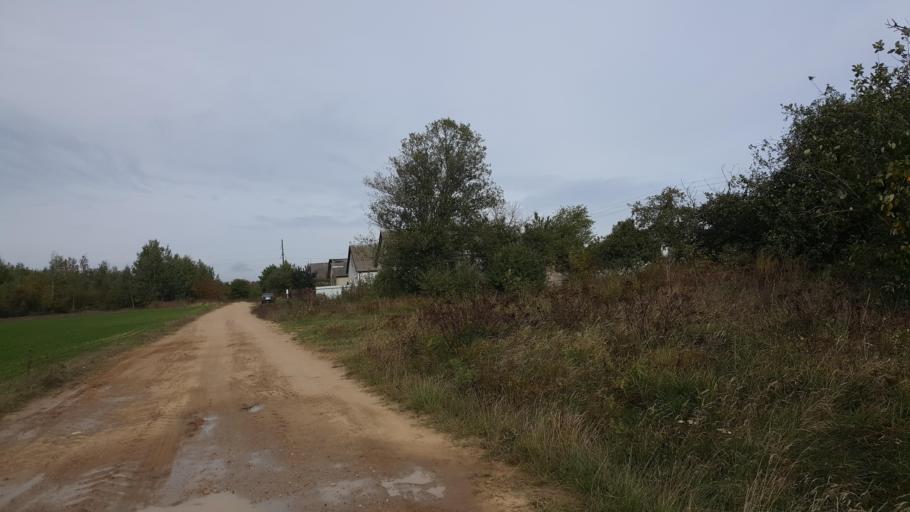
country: BY
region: Brest
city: Kamyanyets
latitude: 52.4110
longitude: 23.8895
